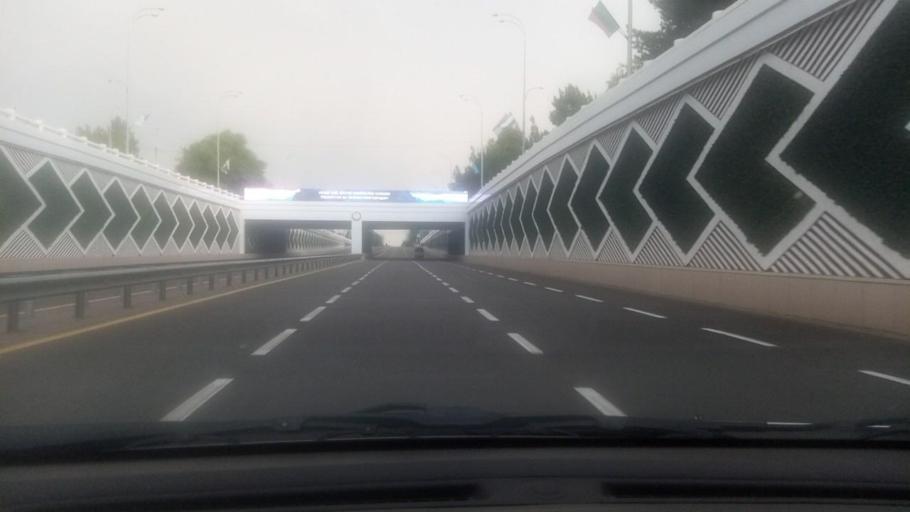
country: UZ
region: Toshkent
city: Salor
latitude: 41.3314
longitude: 69.3509
